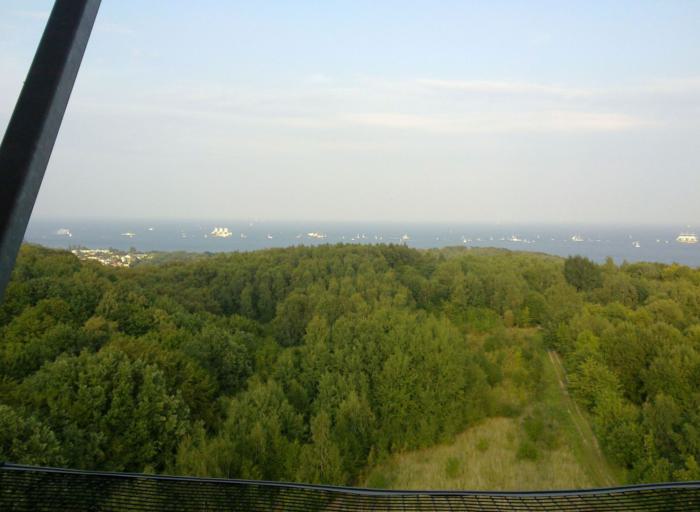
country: PL
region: Pomeranian Voivodeship
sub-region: Sopot
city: Sopot
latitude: 54.4670
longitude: 18.5431
